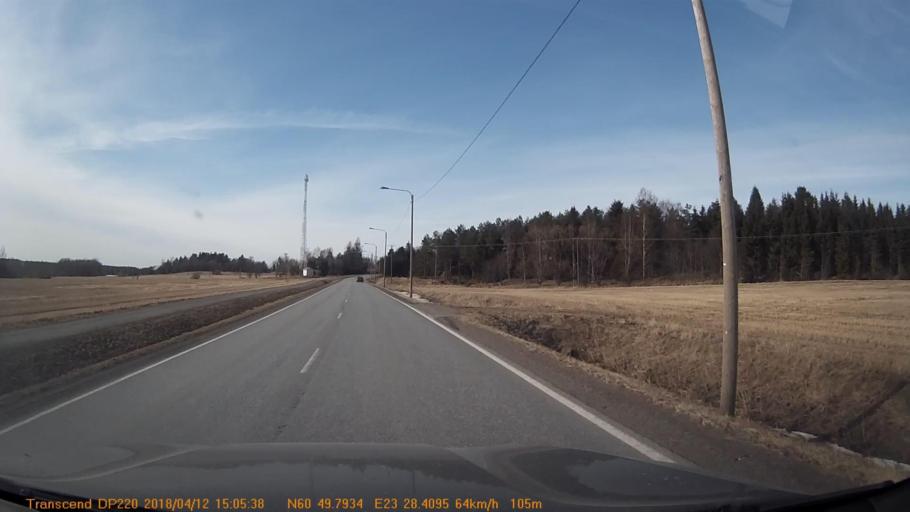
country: FI
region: Haeme
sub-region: Forssa
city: Jokioinen
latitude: 60.8301
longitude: 23.4730
